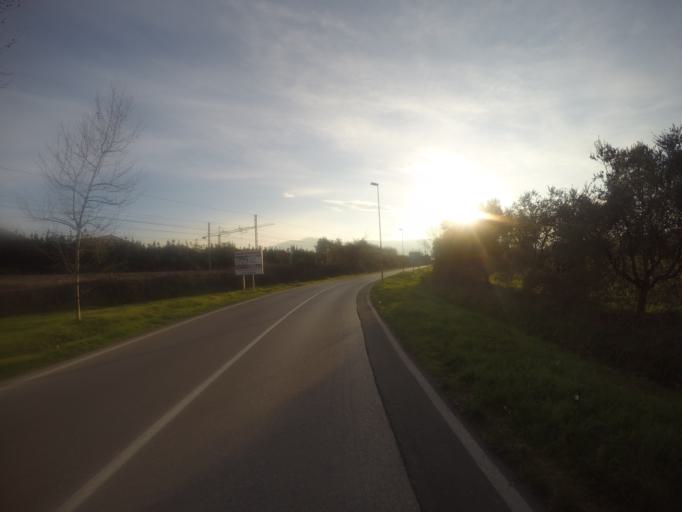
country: IT
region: Tuscany
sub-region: Provincia di Prato
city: Prato
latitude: 43.8924
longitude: 11.0654
